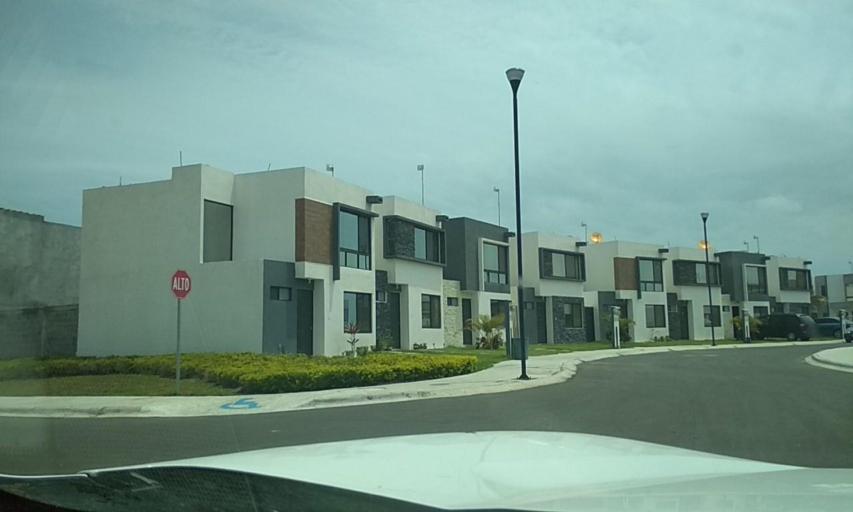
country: MX
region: Veracruz
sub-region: Veracruz
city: Las Amapolas
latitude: 19.1492
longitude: -96.2160
